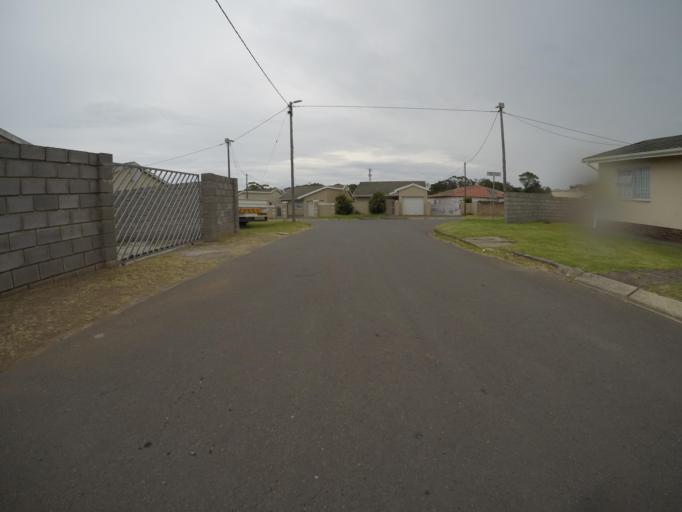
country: ZA
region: Eastern Cape
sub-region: Buffalo City Metropolitan Municipality
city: East London
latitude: -32.9986
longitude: 27.8469
